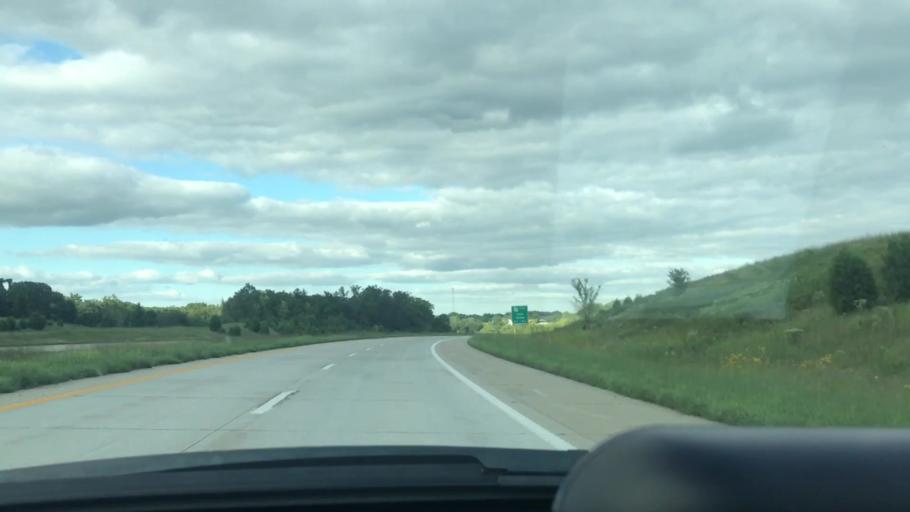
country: US
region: Missouri
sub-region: Benton County
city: Lincoln
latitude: 38.4452
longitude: -93.2926
